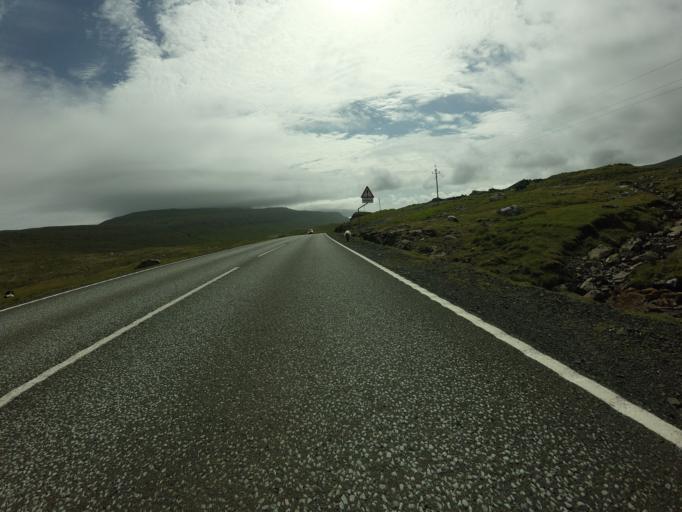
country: FO
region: Sandoy
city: Sandur
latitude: 61.8746
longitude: -6.8577
